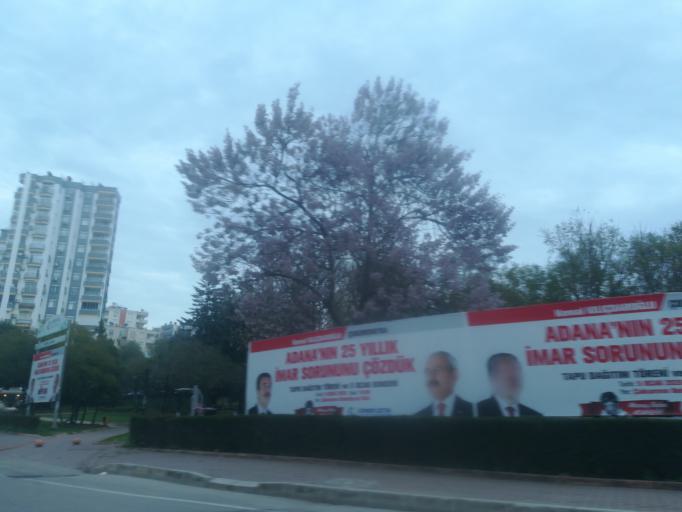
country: TR
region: Adana
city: Adana
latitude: 37.0386
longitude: 35.2934
